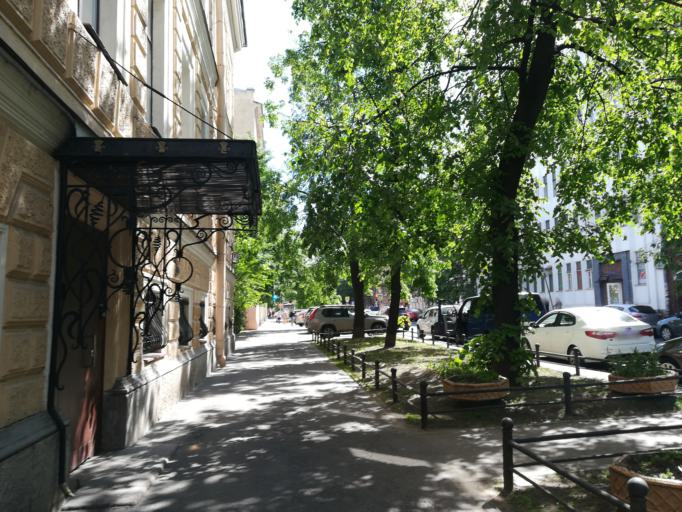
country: RU
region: St.-Petersburg
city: Vasyl'evsky Ostrov
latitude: 59.9464
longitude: 30.2683
